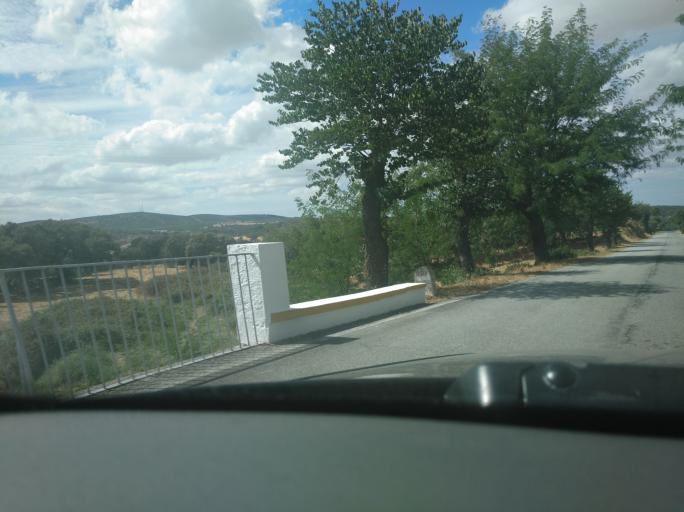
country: PT
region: Portalegre
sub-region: Arronches
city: Arronches
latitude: 39.0574
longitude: -7.4352
